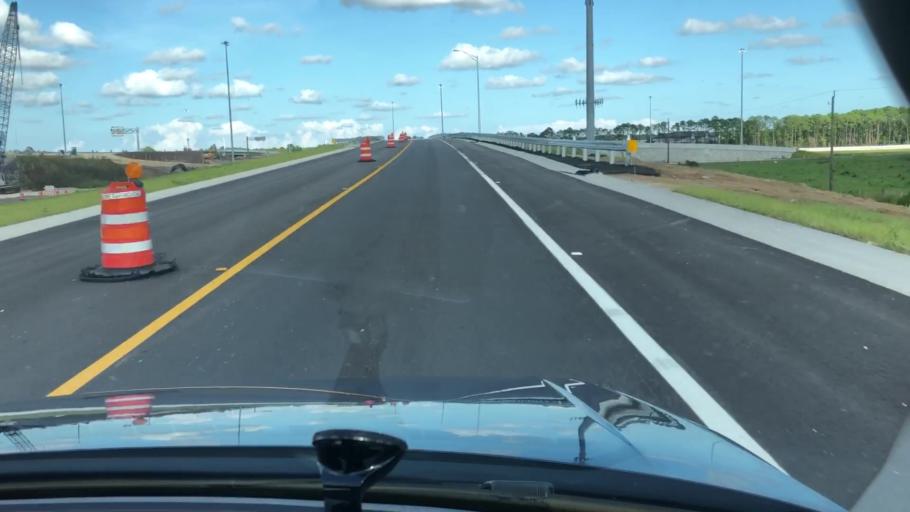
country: US
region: Florida
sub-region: Volusia County
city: South Daytona
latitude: 29.1533
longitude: -81.0794
